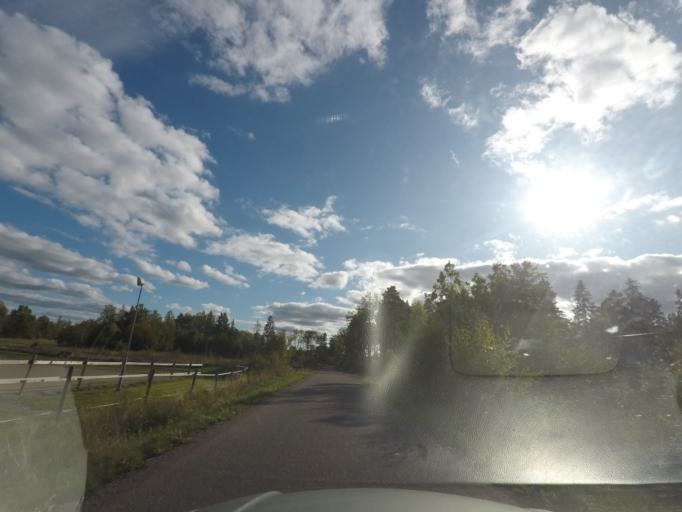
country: SE
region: Vaestmanland
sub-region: Hallstahammars Kommun
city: Kolback
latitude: 59.5060
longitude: 16.1922
